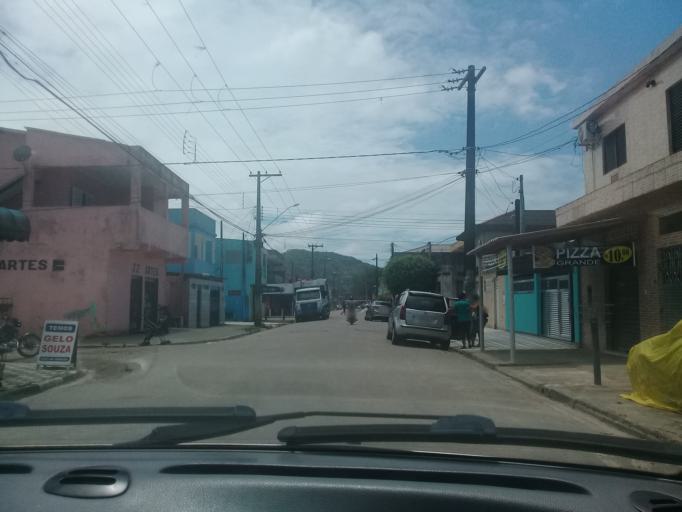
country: BR
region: Sao Paulo
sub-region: Guaruja
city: Guaruja
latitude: -23.9640
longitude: -46.2544
